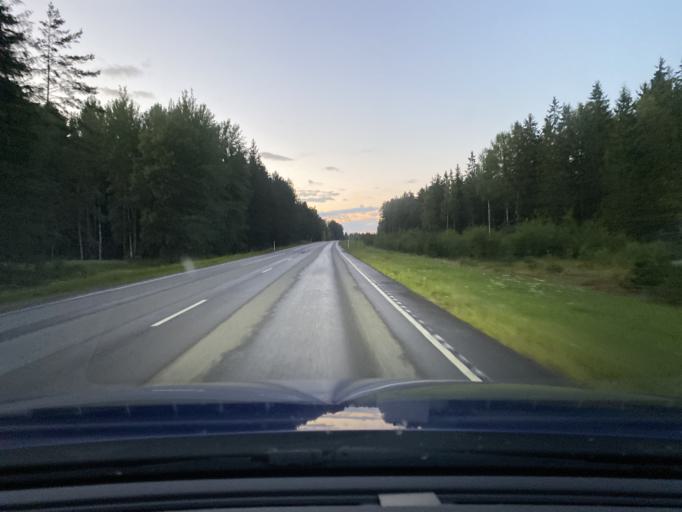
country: FI
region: Varsinais-Suomi
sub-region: Loimaa
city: Aura
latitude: 60.7158
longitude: 22.5711
